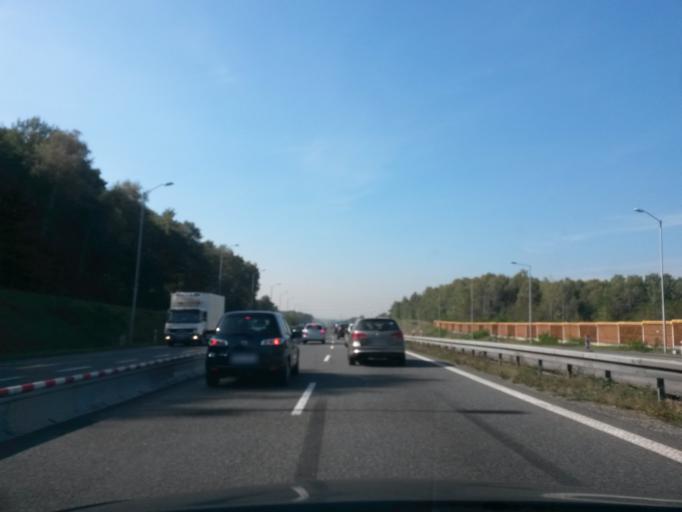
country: PL
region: Silesian Voivodeship
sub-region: Ruda Slaska
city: Ruda Slaska
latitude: 50.2526
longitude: 18.8791
